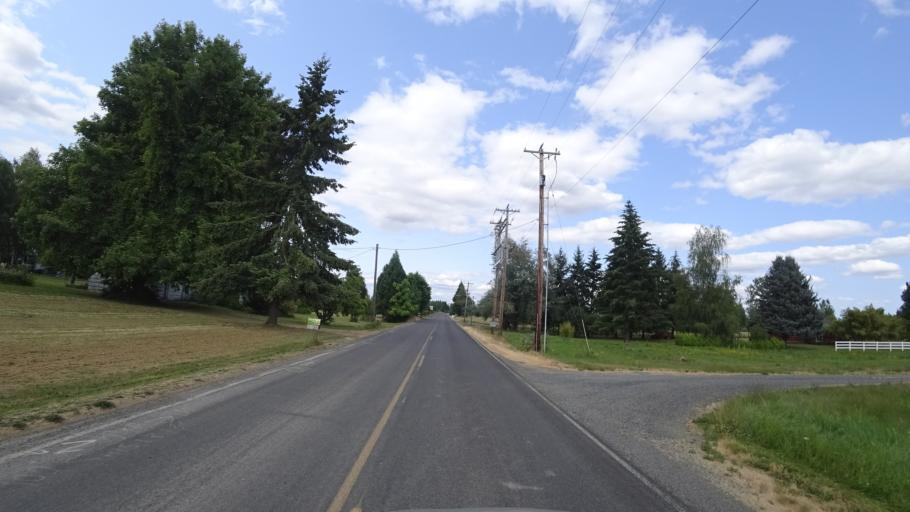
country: US
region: Oregon
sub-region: Washington County
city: Oak Hills
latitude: 45.6363
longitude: -122.7957
